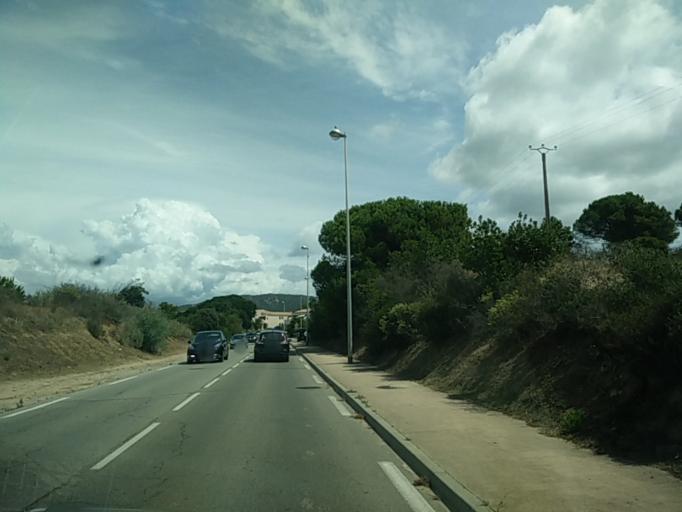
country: FR
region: Corsica
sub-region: Departement de la Corse-du-Sud
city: Pietrosella
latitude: 41.8474
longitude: 8.7850
